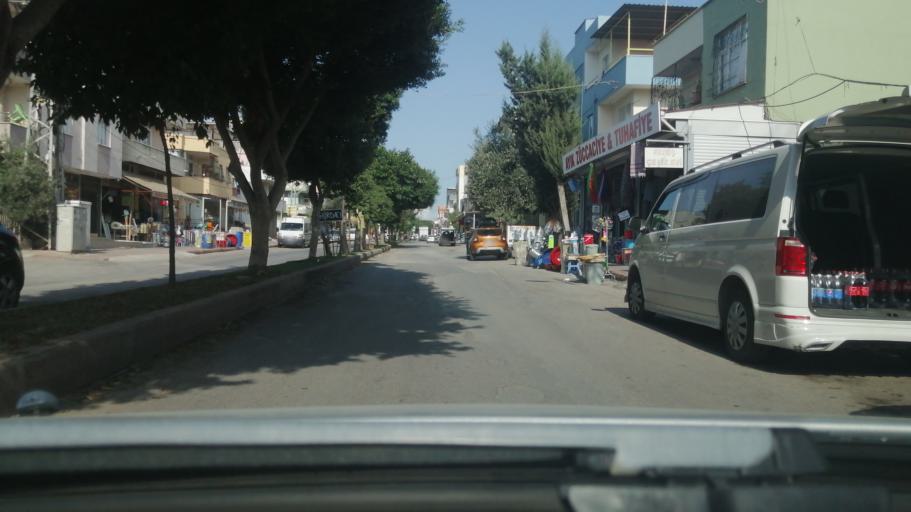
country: TR
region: Adana
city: Seyhan
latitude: 37.0182
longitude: 35.2731
